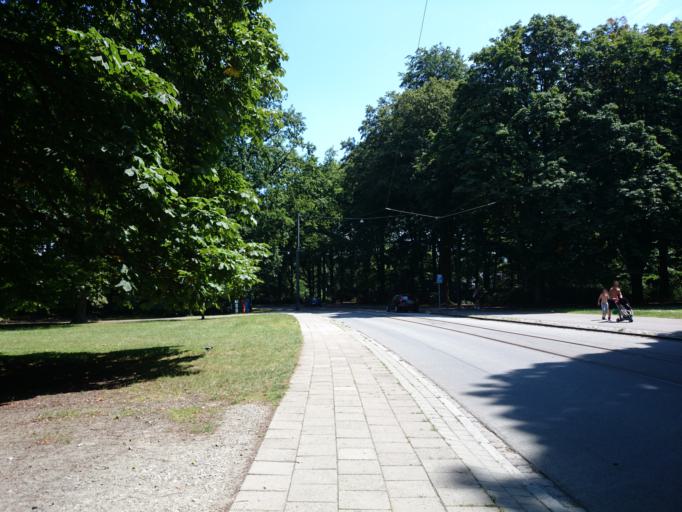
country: SE
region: Skane
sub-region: Malmo
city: Malmoe
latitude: 55.6001
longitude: 12.9862
